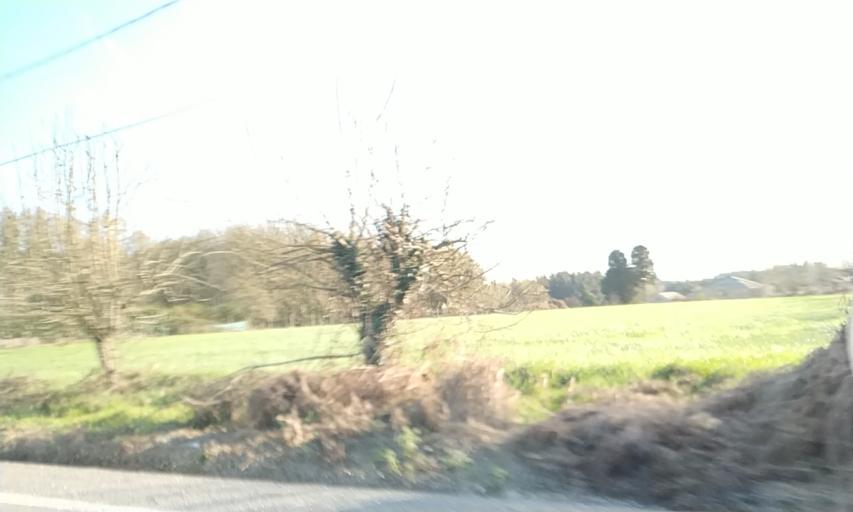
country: ES
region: Galicia
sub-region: Provincia de Lugo
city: Corgo
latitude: 42.9576
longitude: -7.4713
